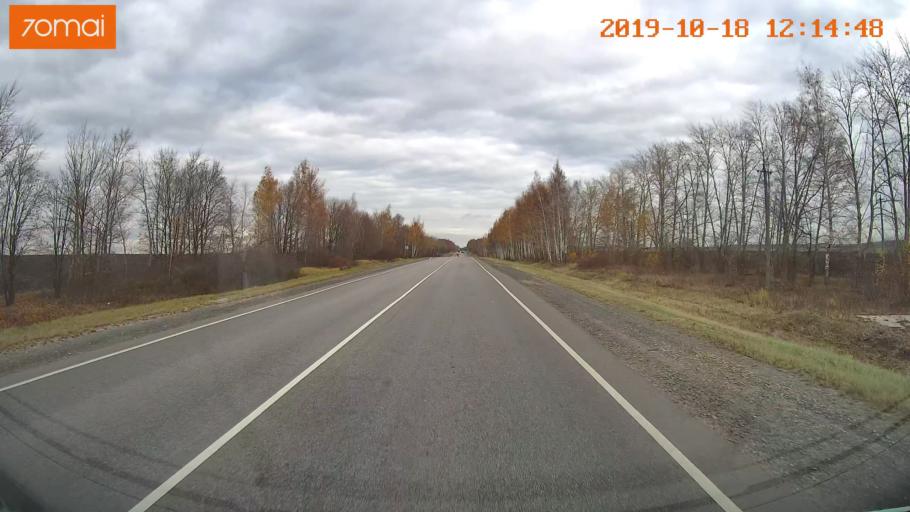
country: RU
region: Rjazan
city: Zakharovo
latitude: 54.4354
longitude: 39.3894
